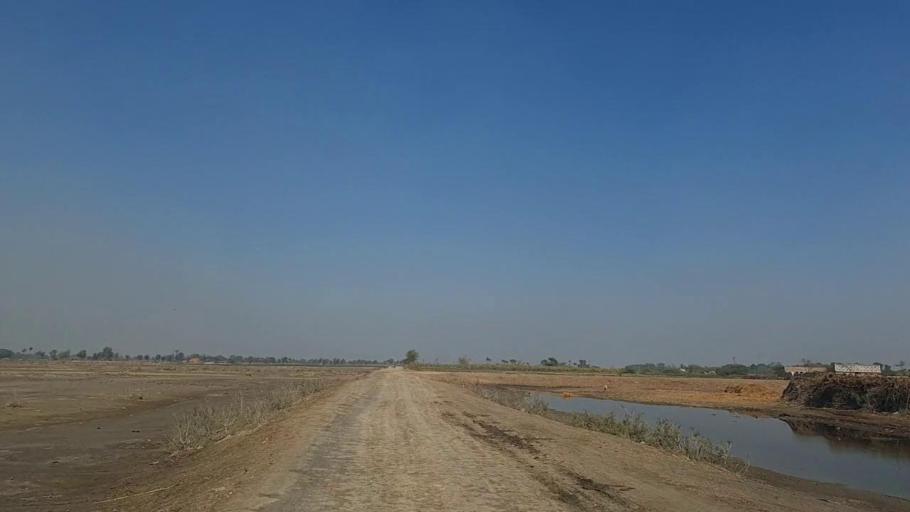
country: PK
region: Sindh
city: Daur
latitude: 26.4767
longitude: 68.3253
